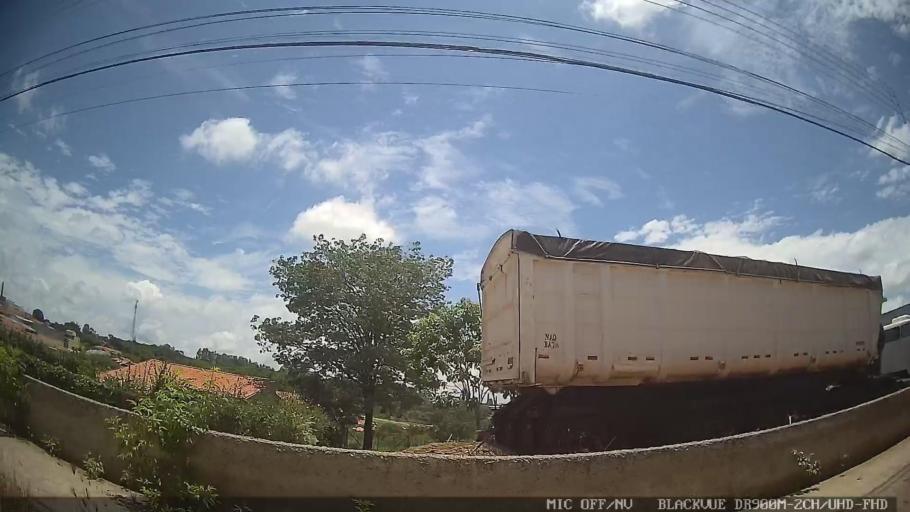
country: BR
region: Sao Paulo
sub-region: Laranjal Paulista
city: Laranjal Paulista
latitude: -23.0441
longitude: -47.8301
